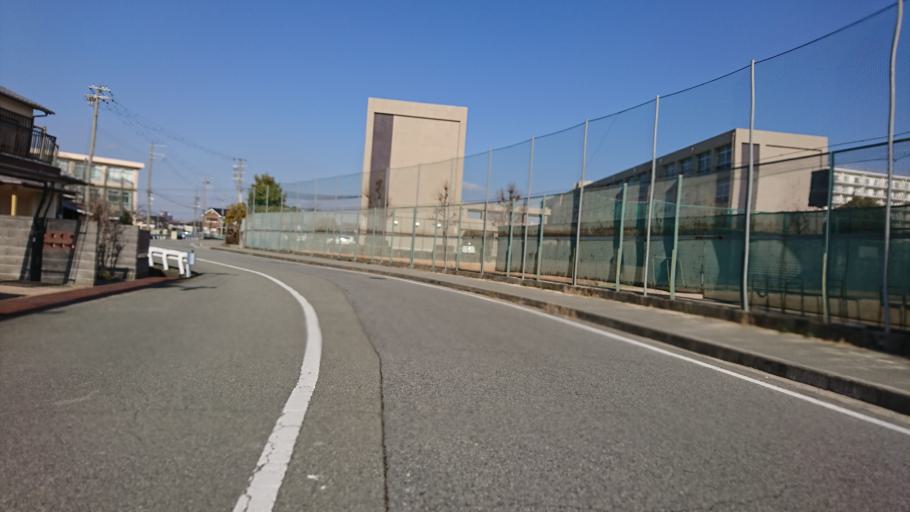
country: JP
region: Hyogo
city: Kakogawacho-honmachi
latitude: 34.7328
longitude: 134.8626
